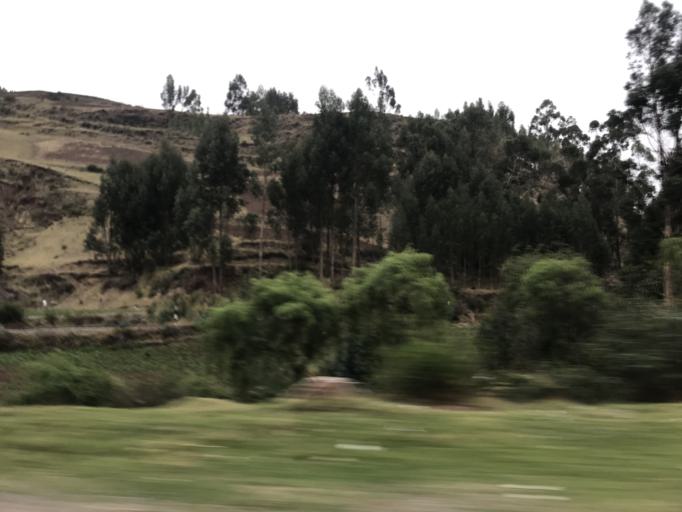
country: PE
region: Cusco
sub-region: Provincia de Anta
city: Huarocondo
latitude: -13.3984
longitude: -72.2109
